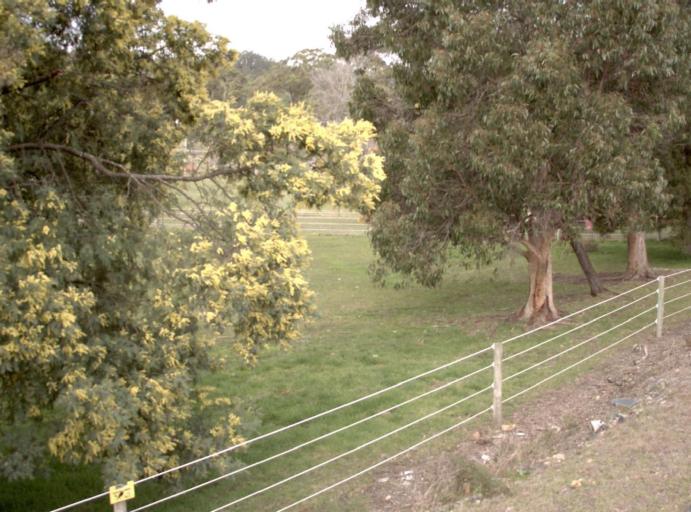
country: AU
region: Tasmania
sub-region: Launceston
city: Mayfield
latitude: -41.2633
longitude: 147.1605
